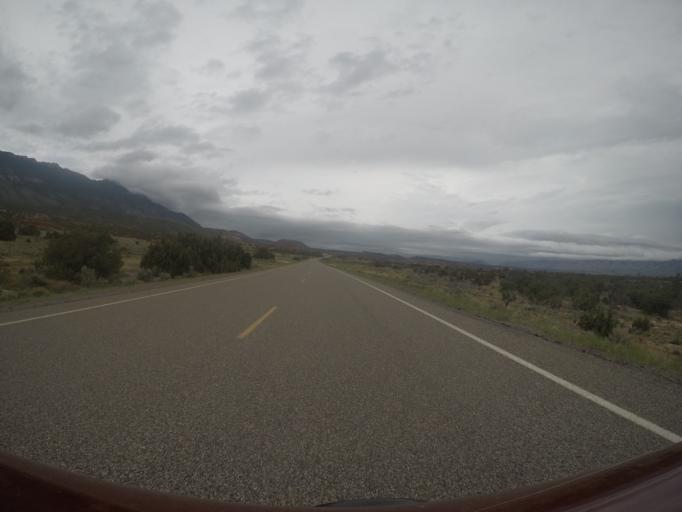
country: US
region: Wyoming
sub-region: Big Horn County
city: Lovell
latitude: 45.0861
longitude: -108.2513
